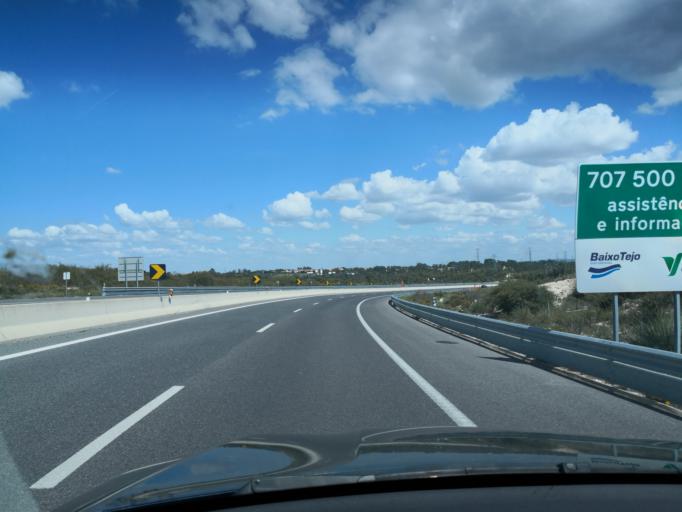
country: PT
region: Setubal
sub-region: Seixal
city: Corroios
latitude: 38.6122
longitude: -9.1578
